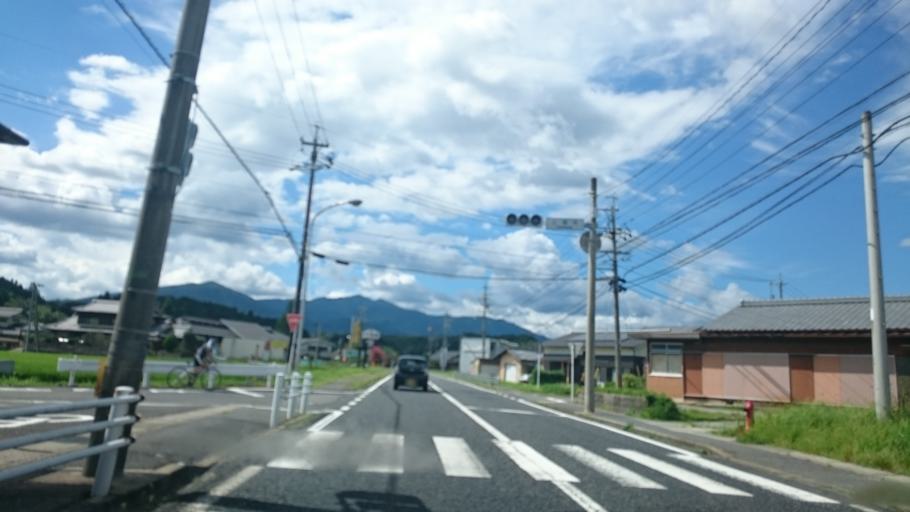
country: JP
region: Gifu
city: Nakatsugawa
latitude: 35.5258
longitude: 137.4685
